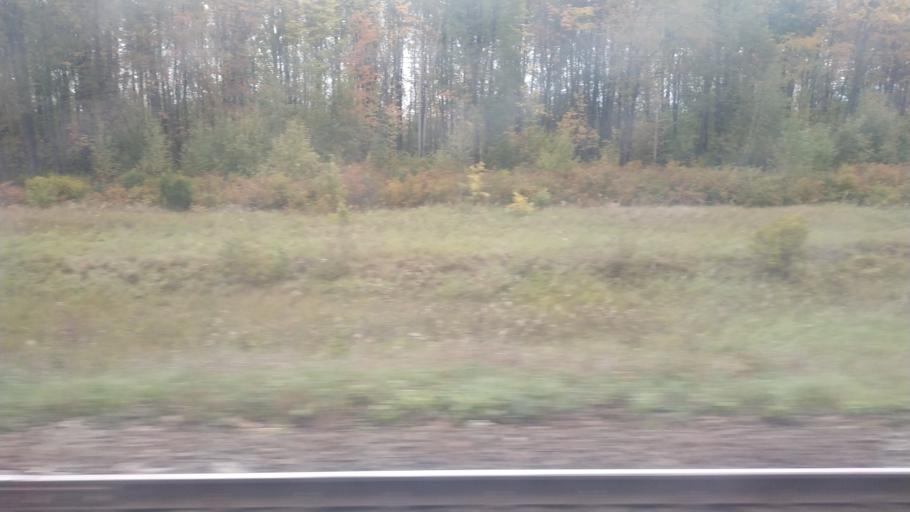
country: RU
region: Moskovskaya
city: Ozherel'ye
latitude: 54.7575
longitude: 38.3319
